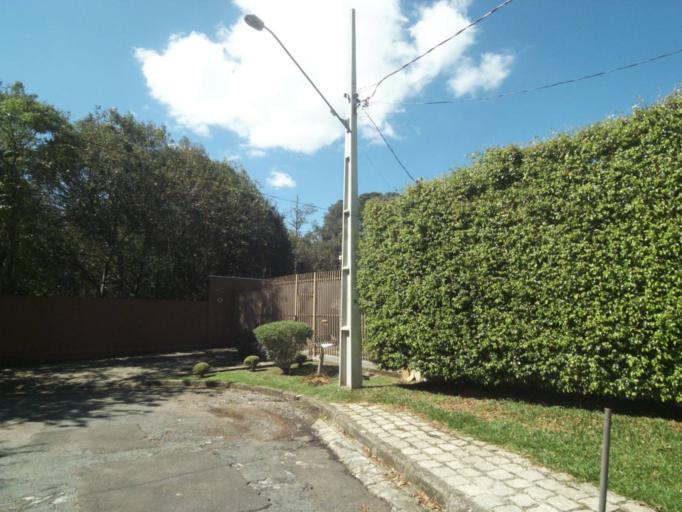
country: BR
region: Parana
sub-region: Curitiba
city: Curitiba
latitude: -25.3970
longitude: -49.2673
